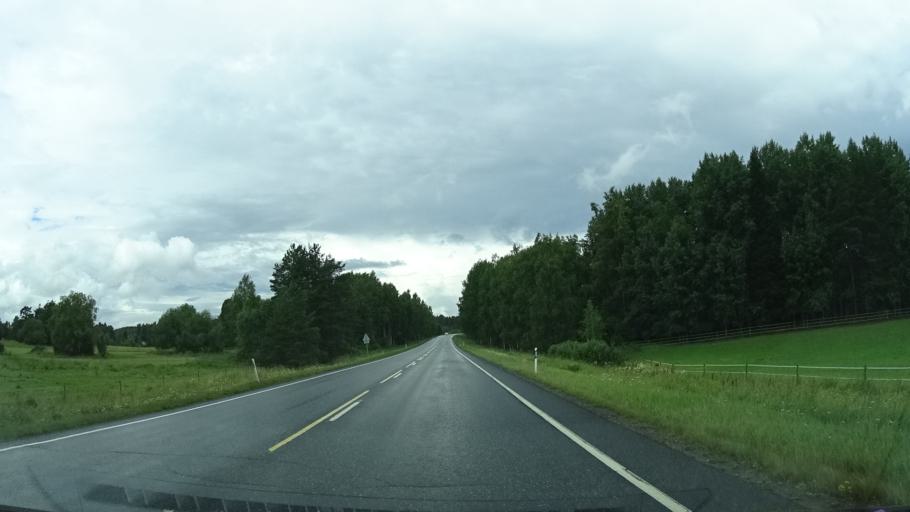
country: FI
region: Haeme
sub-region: Haemeenlinna
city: Kalvola
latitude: 61.1612
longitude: 24.0433
